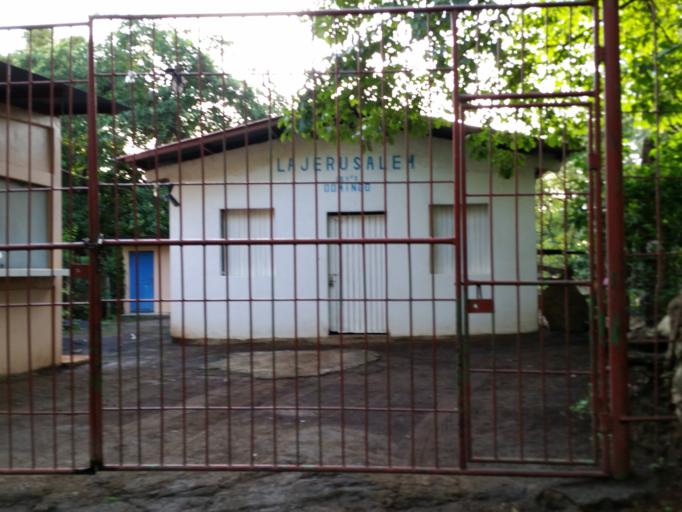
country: NI
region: Managua
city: Managua
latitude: 12.0753
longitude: -86.2439
